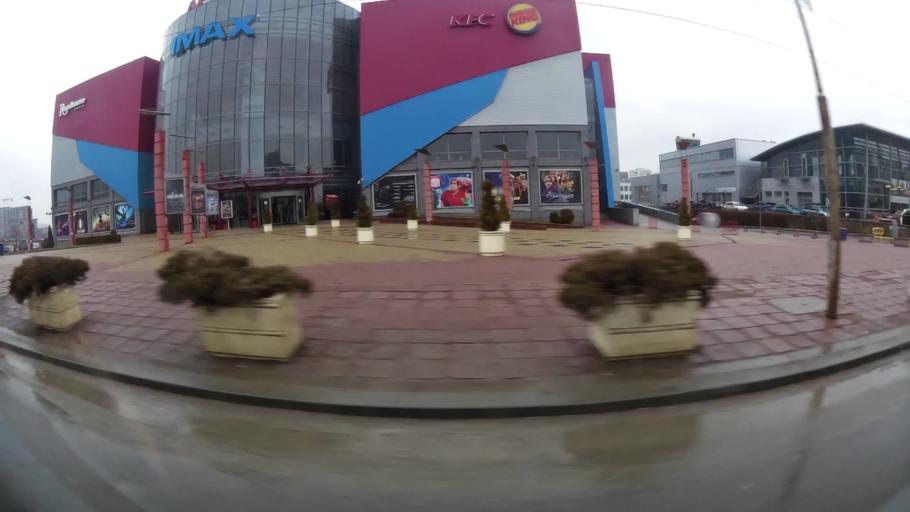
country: BG
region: Sofia-Capital
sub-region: Stolichna Obshtina
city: Sofia
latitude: 42.6241
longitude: 23.3770
